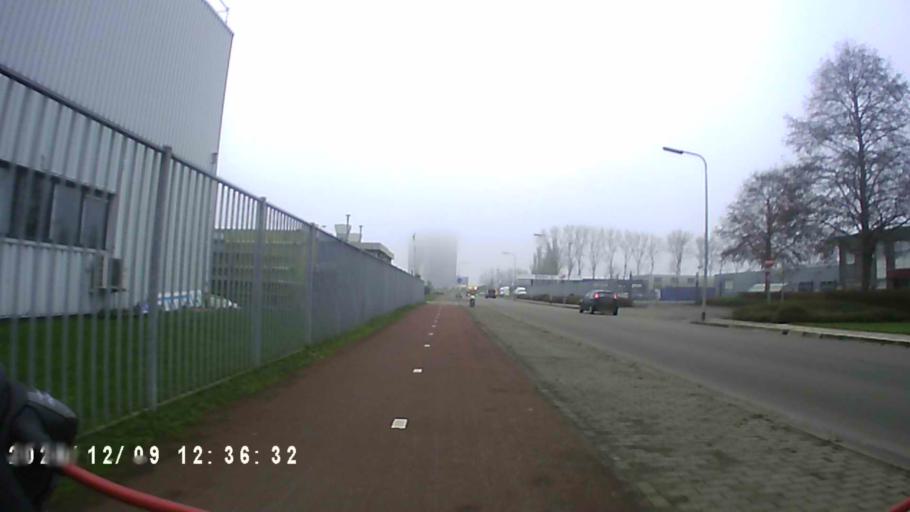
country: NL
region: Groningen
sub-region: Gemeente Groningen
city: Oosterpark
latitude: 53.2194
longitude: 6.6033
